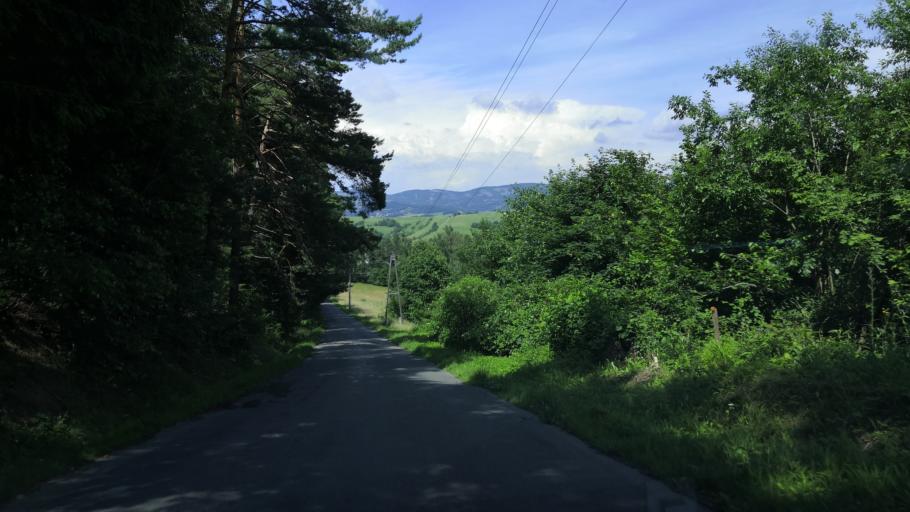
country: CZ
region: Zlin
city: Vidce
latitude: 49.4331
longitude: 18.0944
